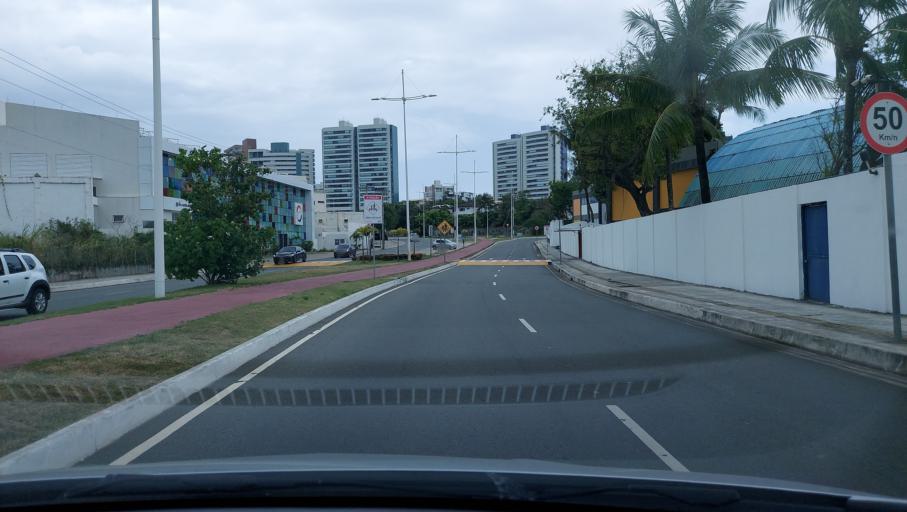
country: BR
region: Bahia
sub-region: Lauro De Freitas
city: Lauro de Freitas
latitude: -12.9568
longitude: -38.4000
